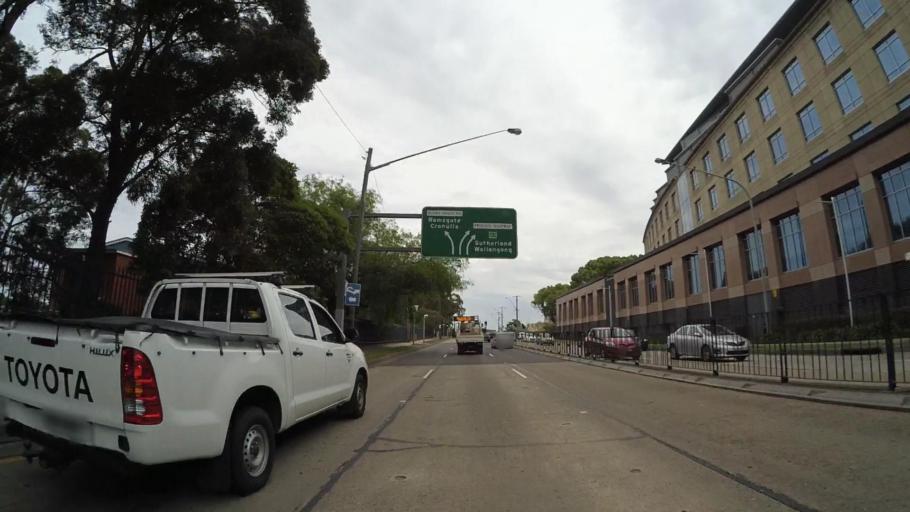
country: AU
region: New South Wales
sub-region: Kogarah
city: Beverly Park
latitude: -33.9669
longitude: 151.1367
